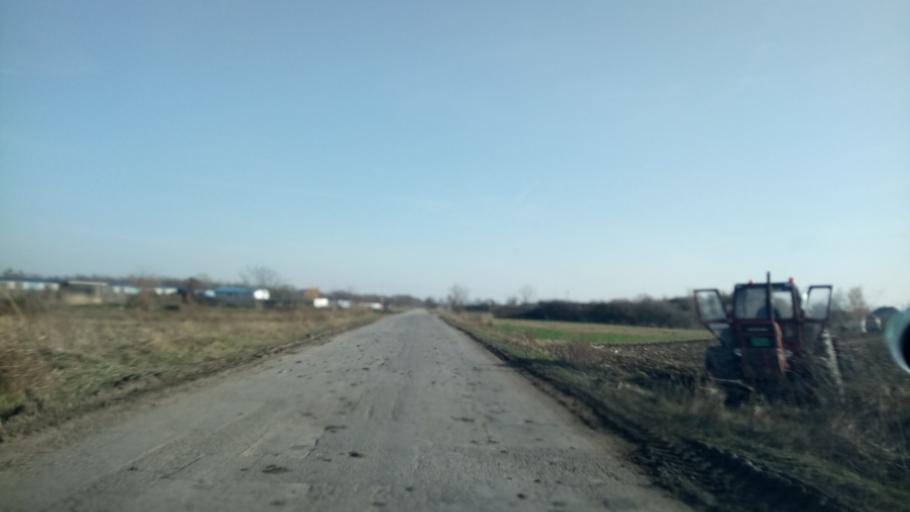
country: RS
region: Autonomna Pokrajina Vojvodina
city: Nova Pazova
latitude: 44.9553
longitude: 20.2235
